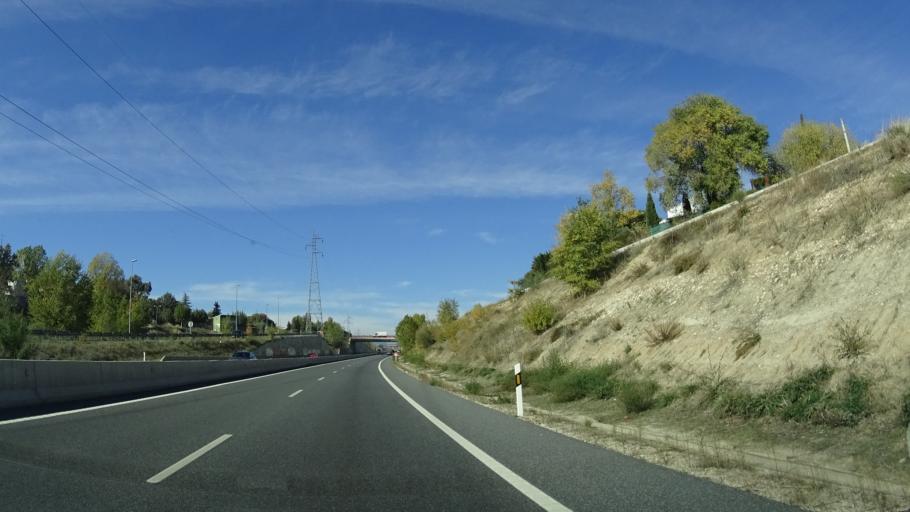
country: ES
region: Madrid
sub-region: Provincia de Madrid
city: Villanueva del Pardillo
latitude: 40.4859
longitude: -3.9432
